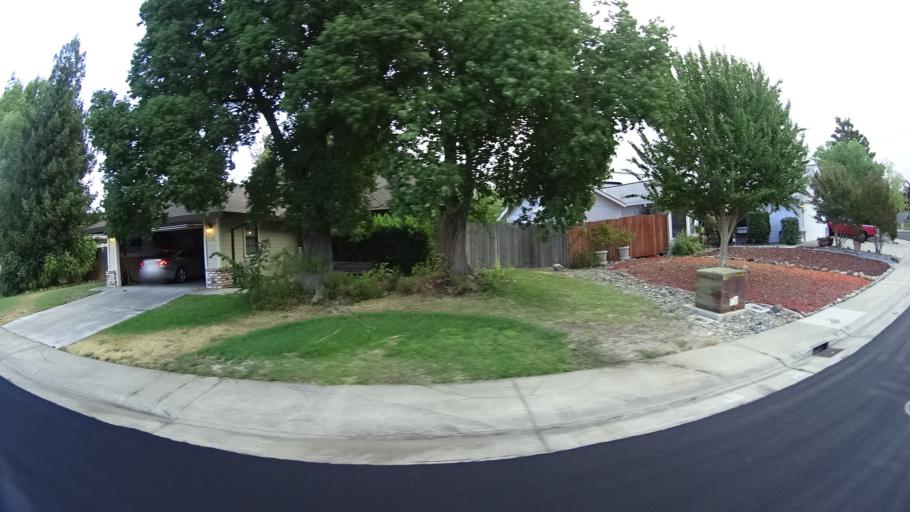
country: US
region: California
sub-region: Sacramento County
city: Laguna
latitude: 38.4276
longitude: -121.4464
